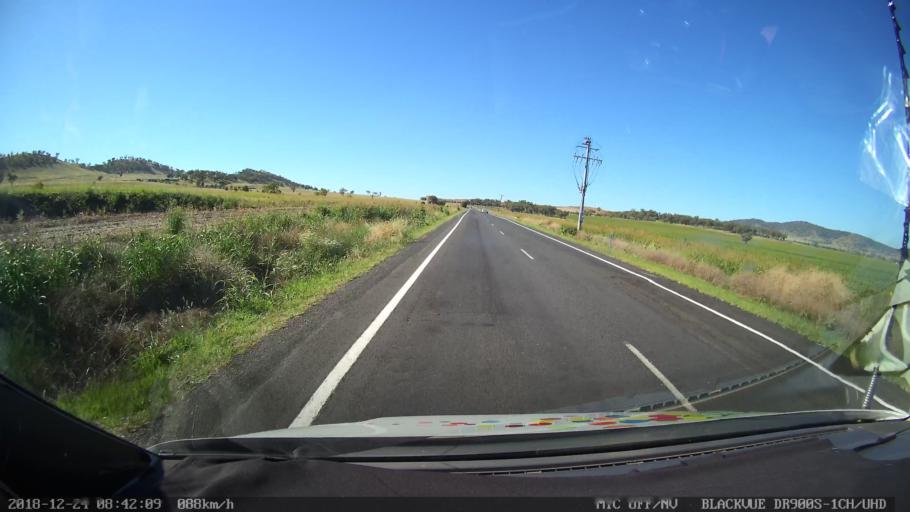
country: AU
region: New South Wales
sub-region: Liverpool Plains
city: Quirindi
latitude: -31.3705
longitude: 150.6435
